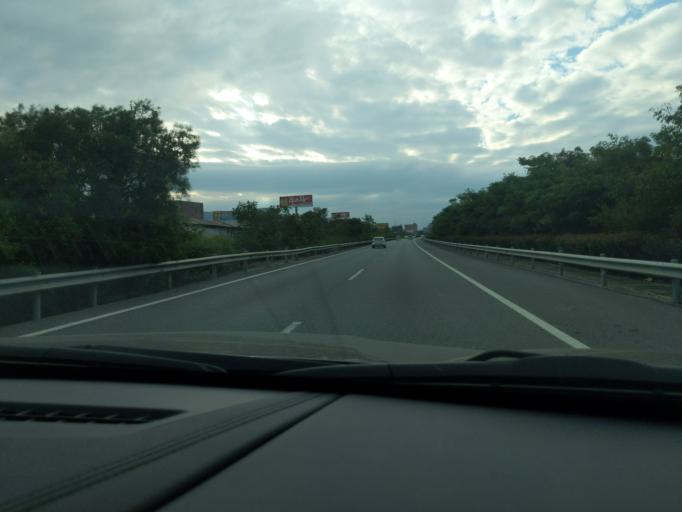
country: CN
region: Fujian
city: Dongshi
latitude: 24.6975
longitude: 118.3625
